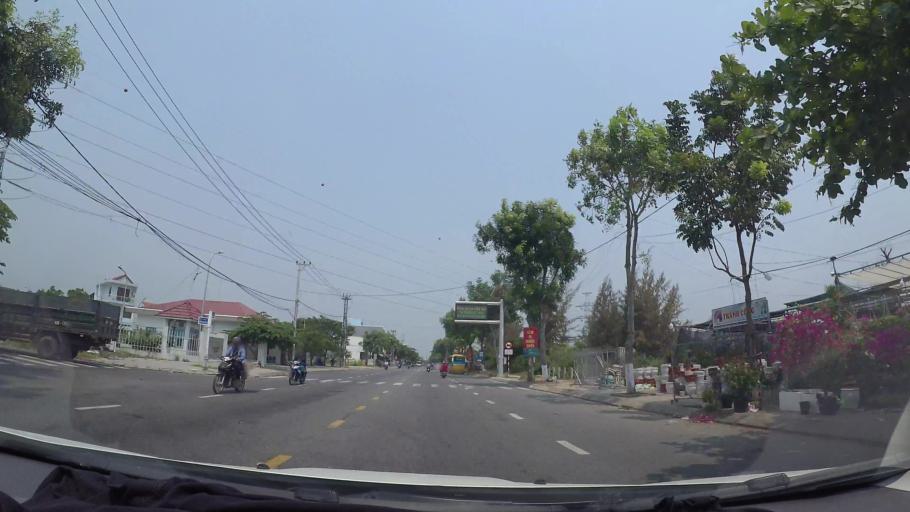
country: VN
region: Da Nang
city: Cam Le
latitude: 15.9961
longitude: 108.2073
